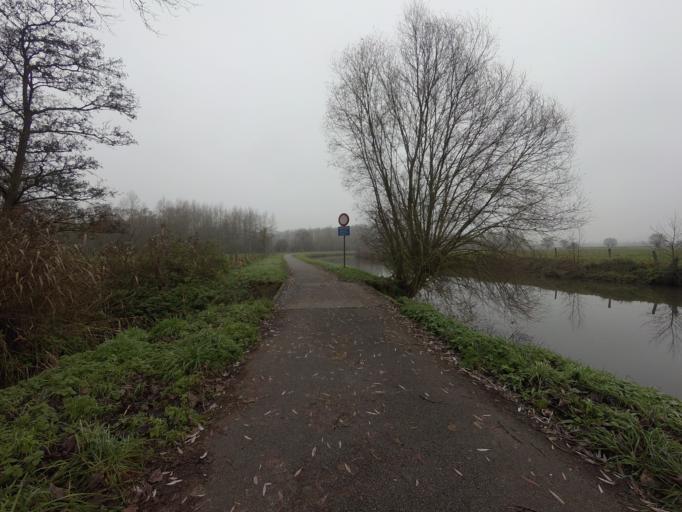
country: BE
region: Flanders
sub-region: Provincie Oost-Vlaanderen
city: Geraardsbergen
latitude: 50.7473
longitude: 3.8557
